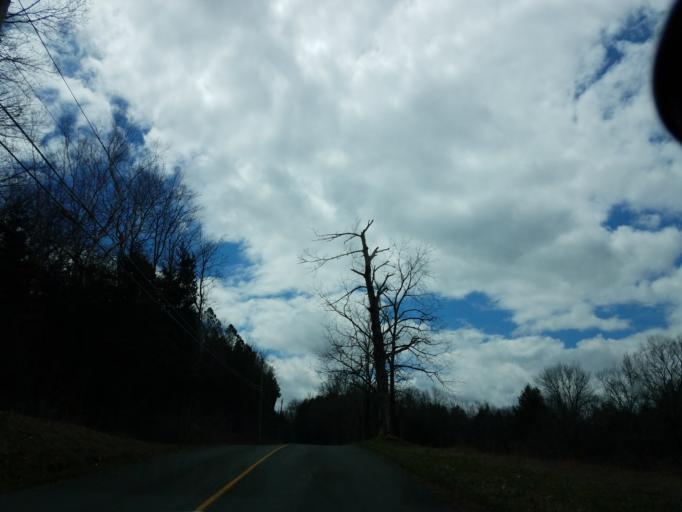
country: US
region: Connecticut
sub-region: Litchfield County
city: Litchfield
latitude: 41.7814
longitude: -73.1771
